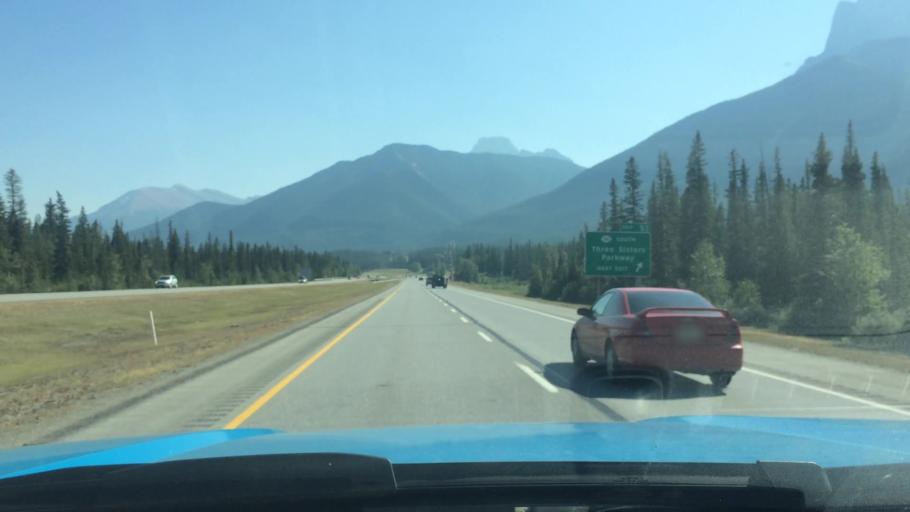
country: CA
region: Alberta
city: Canmore
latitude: 51.0668
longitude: -115.3258
